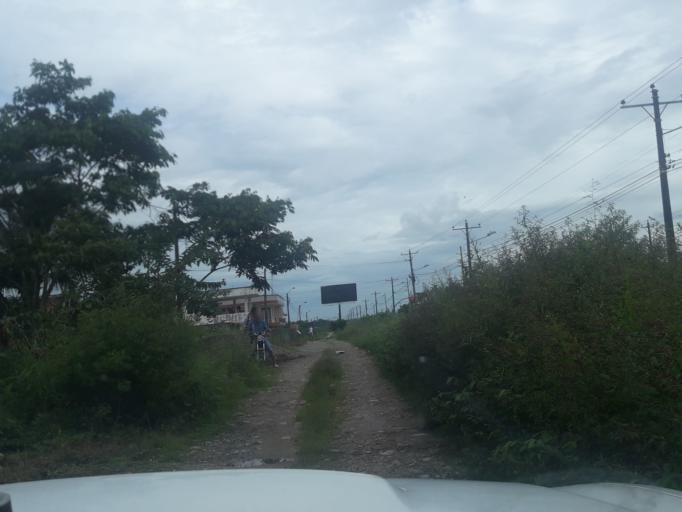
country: EC
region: Napo
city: Archidona
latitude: -0.9460
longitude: -77.8173
